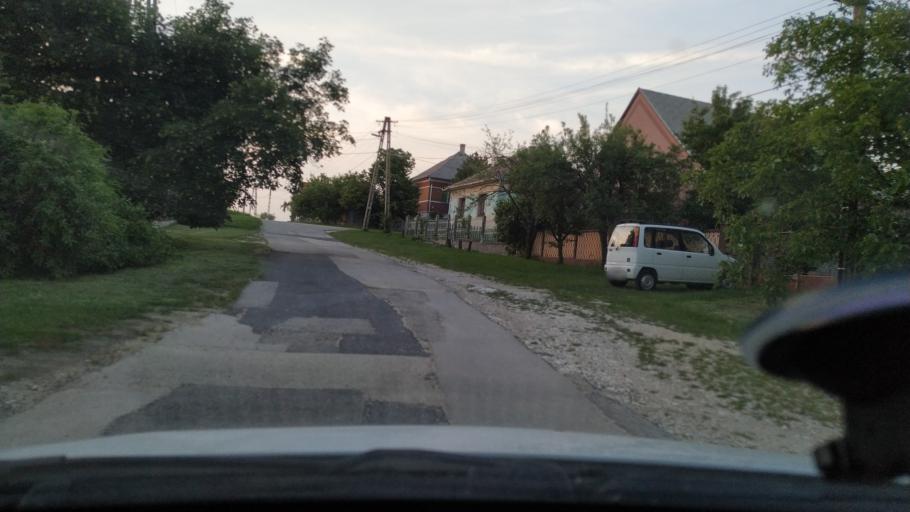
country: HU
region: Veszprem
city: Varpalota
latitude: 47.2046
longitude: 18.1796
